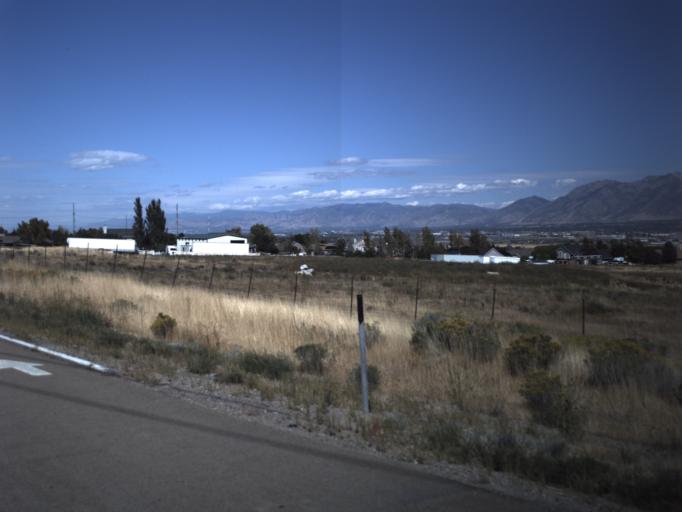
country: US
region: Utah
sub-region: Salt Lake County
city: Bluffdale
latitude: 40.4621
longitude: -111.9425
